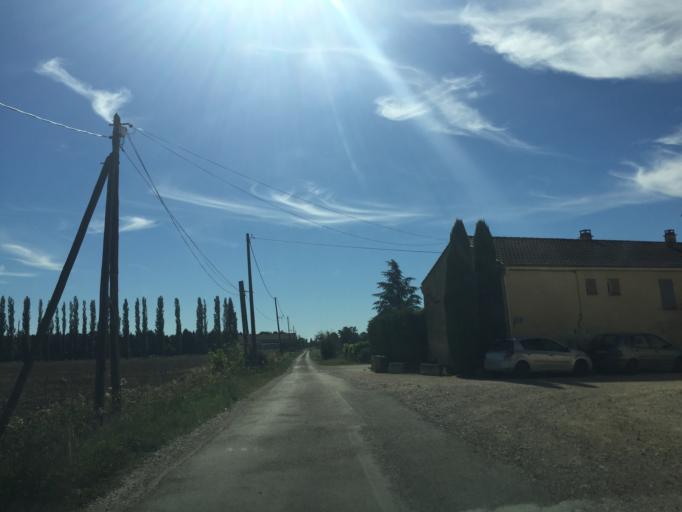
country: FR
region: Provence-Alpes-Cote d'Azur
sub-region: Departement du Vaucluse
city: Piolenc
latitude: 44.1547
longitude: 4.7425
